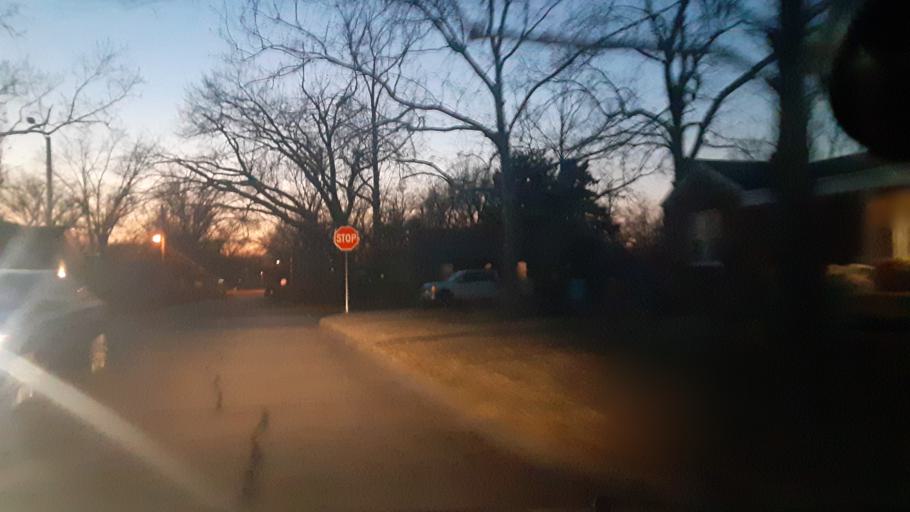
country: US
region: Oklahoma
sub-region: Payne County
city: Stillwater
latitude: 36.1113
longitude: -97.0779
